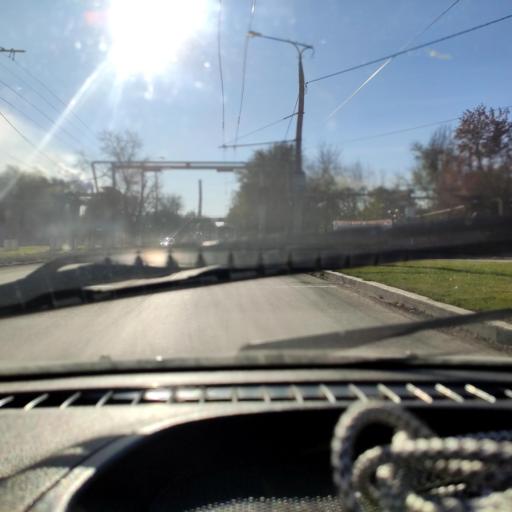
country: RU
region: Samara
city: Tol'yatti
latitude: 53.5610
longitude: 49.4542
